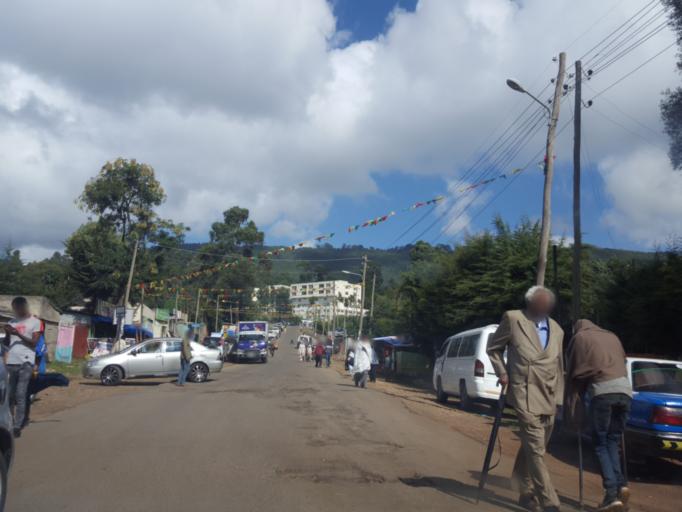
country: ET
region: Adis Abeba
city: Addis Ababa
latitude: 9.0710
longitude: 38.7603
